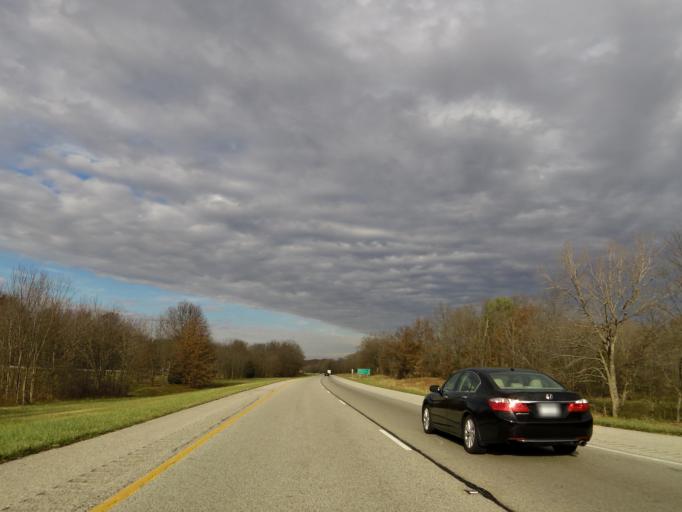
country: US
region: Illinois
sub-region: Washington County
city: Nashville
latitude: 38.3951
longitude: -89.3869
